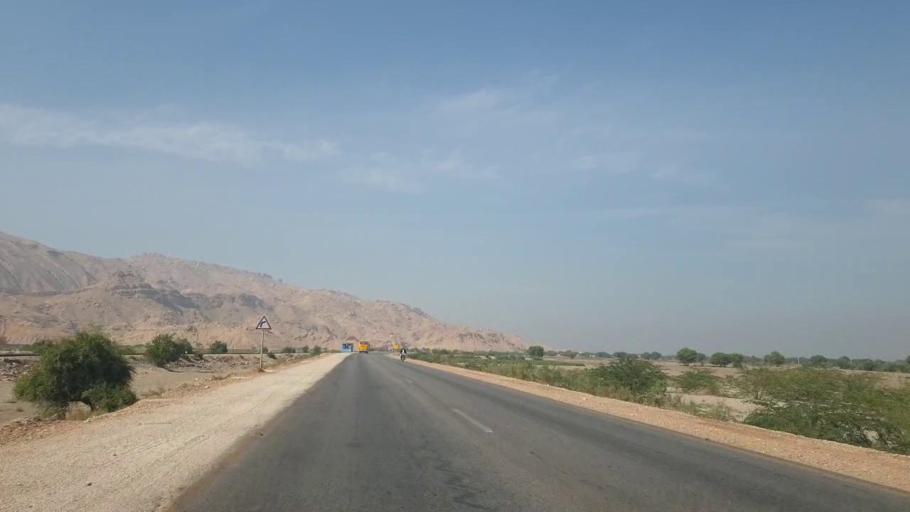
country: PK
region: Sindh
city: Sehwan
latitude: 26.2789
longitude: 67.8972
